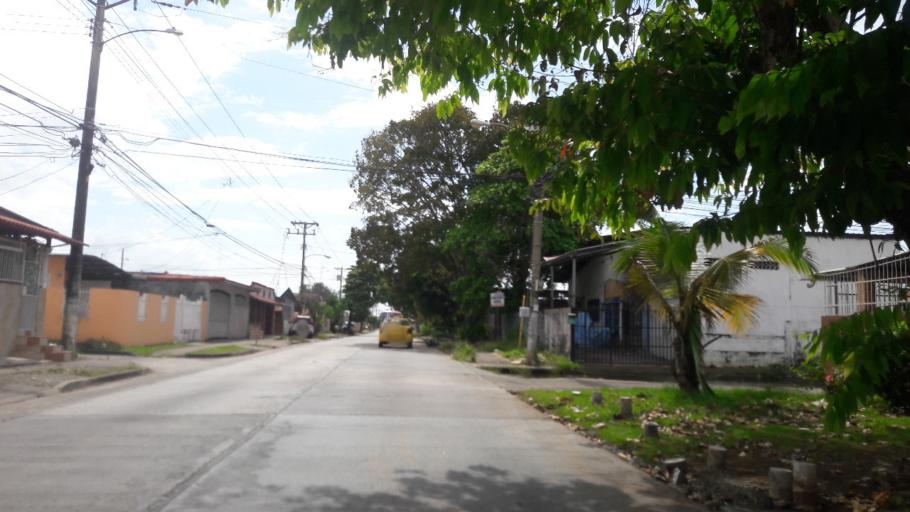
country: PA
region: Panama
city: Tocumen
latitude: 9.0564
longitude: -79.4178
